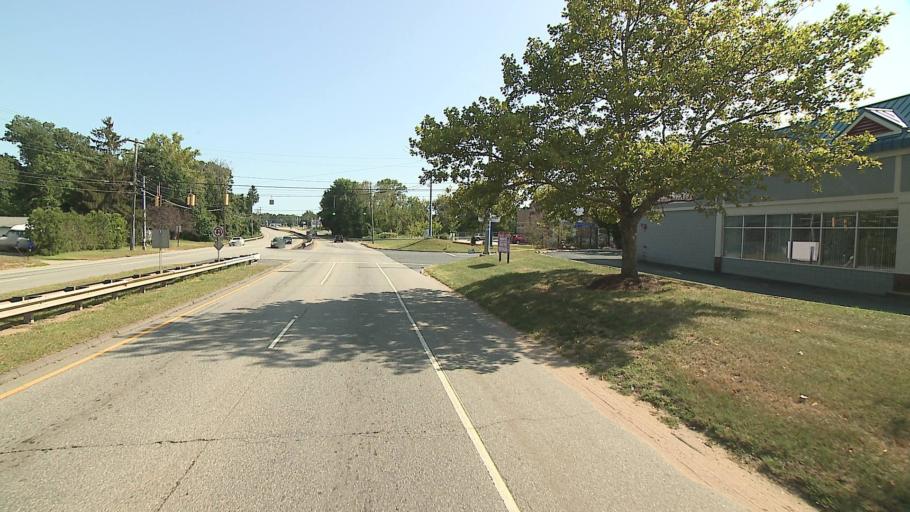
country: US
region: Connecticut
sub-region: Hartford County
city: East Hartford
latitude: 41.7960
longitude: -72.6211
